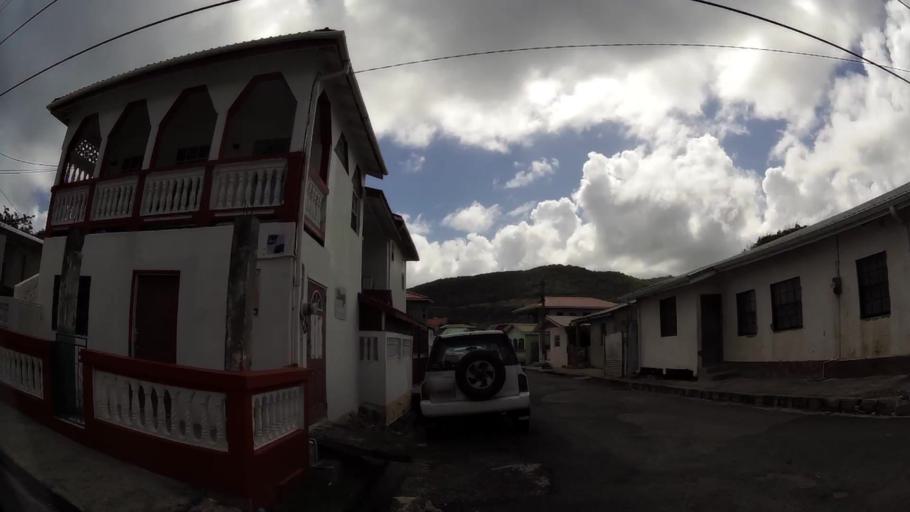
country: LC
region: Dennery Quarter
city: Dennery
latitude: 13.9112
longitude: -60.8901
